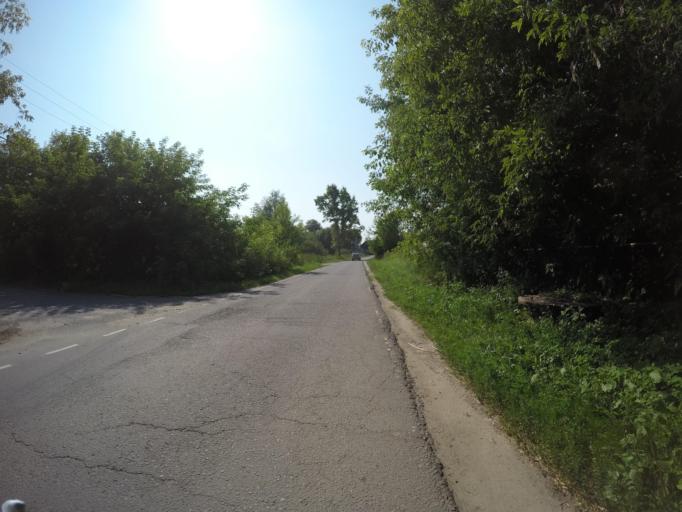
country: RU
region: Moskovskaya
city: Rechitsy
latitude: 55.6166
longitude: 38.5369
